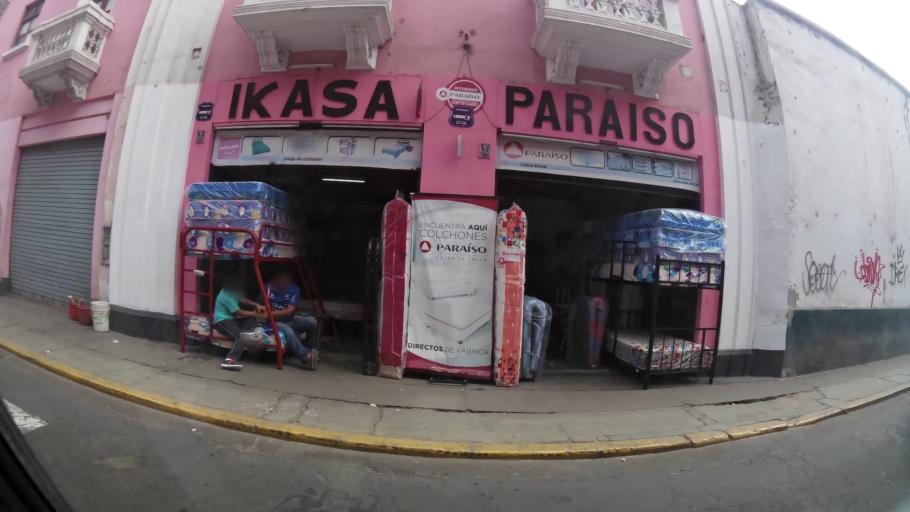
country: PE
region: La Libertad
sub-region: Provincia de Trujillo
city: Trujillo
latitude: -8.1083
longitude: -79.0251
